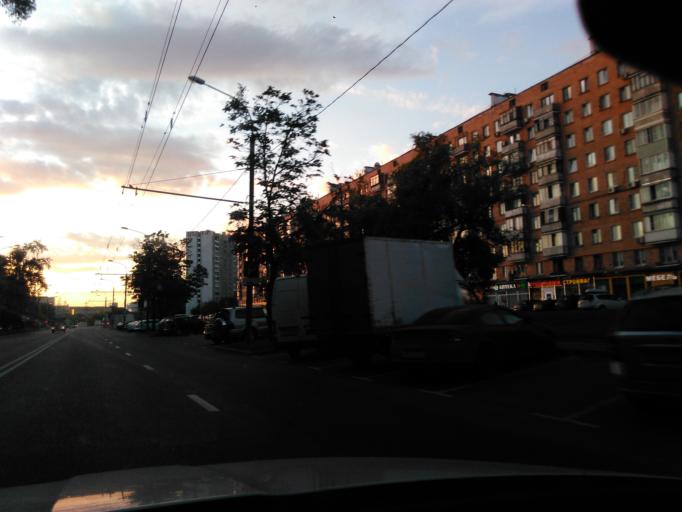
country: RU
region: Moscow
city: Zapadnoye Degunino
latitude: 55.8812
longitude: 37.5200
